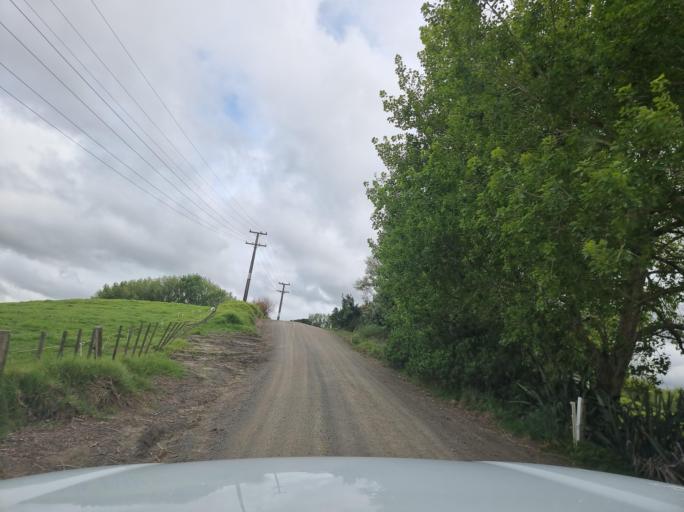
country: NZ
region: Northland
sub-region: Whangarei
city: Ruakaka
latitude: -36.1288
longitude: 174.2084
